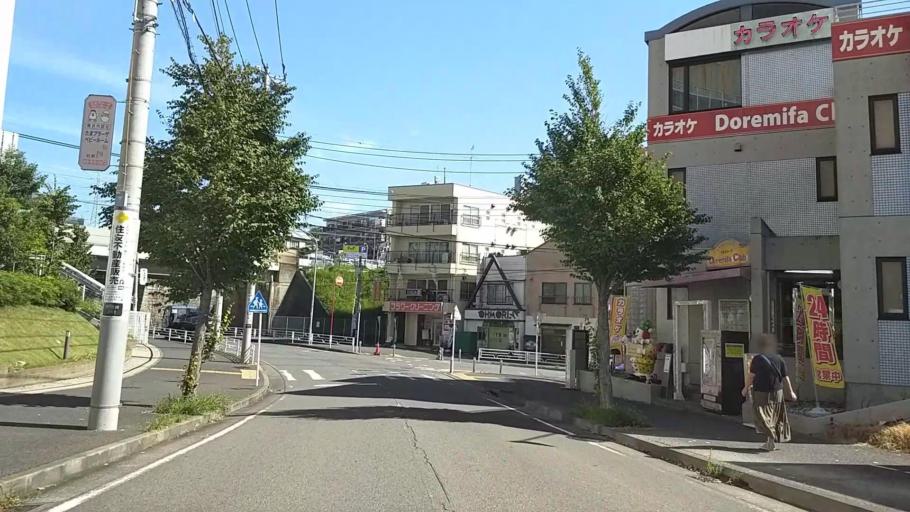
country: JP
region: Tokyo
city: Chofugaoka
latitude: 35.5772
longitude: 139.5600
